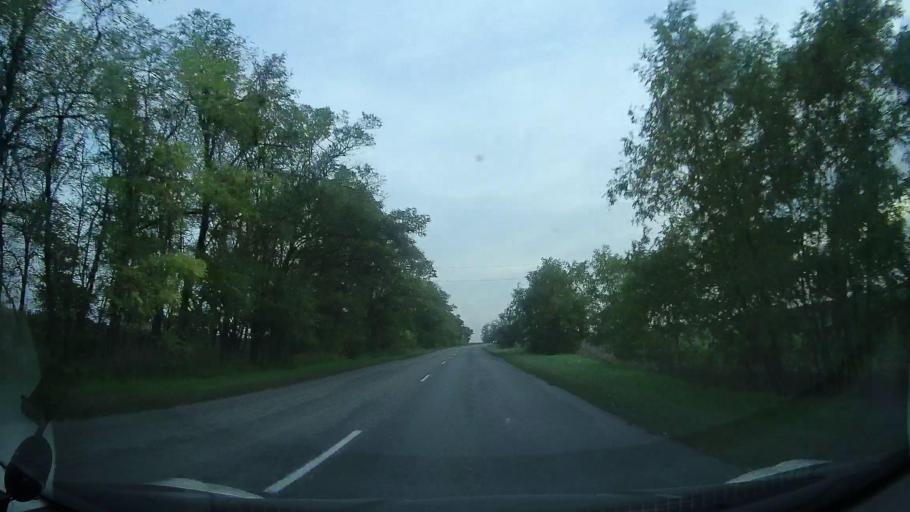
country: RU
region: Rostov
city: Ol'ginskaya
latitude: 47.1095
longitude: 39.9776
